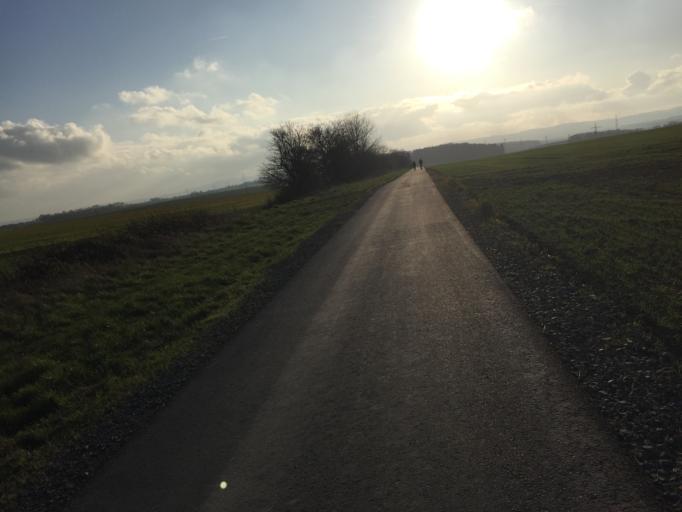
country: DE
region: Hesse
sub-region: Regierungsbezirk Giessen
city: Langgons
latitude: 50.5143
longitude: 8.7108
